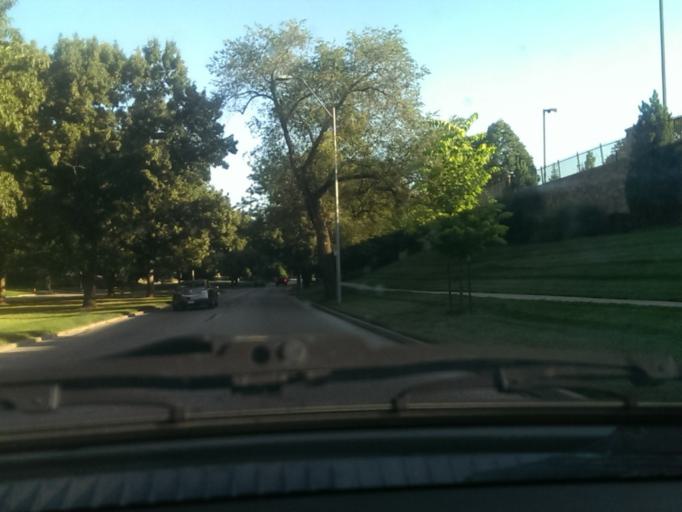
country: US
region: Kansas
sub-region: Johnson County
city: Leawood
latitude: 38.9698
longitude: -94.6051
